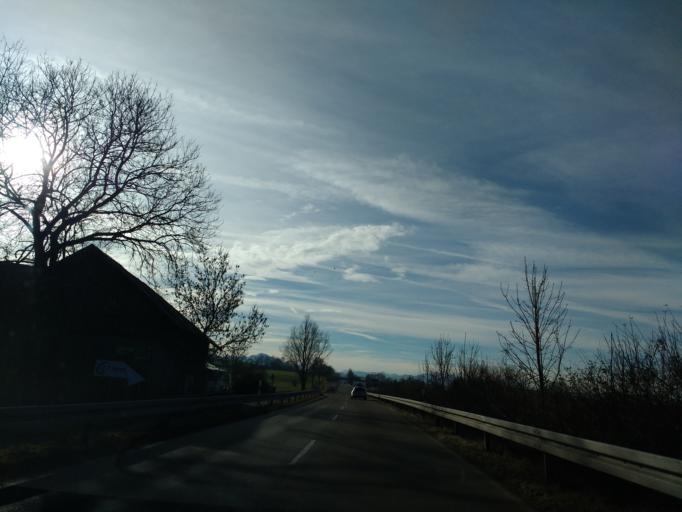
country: DE
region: Bavaria
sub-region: Swabia
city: Wildpoldsried
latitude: 47.7543
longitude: 10.3909
